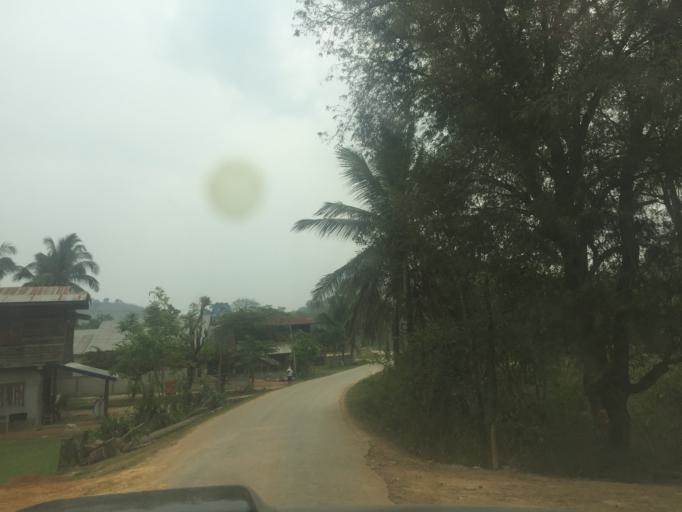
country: LA
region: Vientiane
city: Muang Sanakham
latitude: 18.4004
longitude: 101.5165
